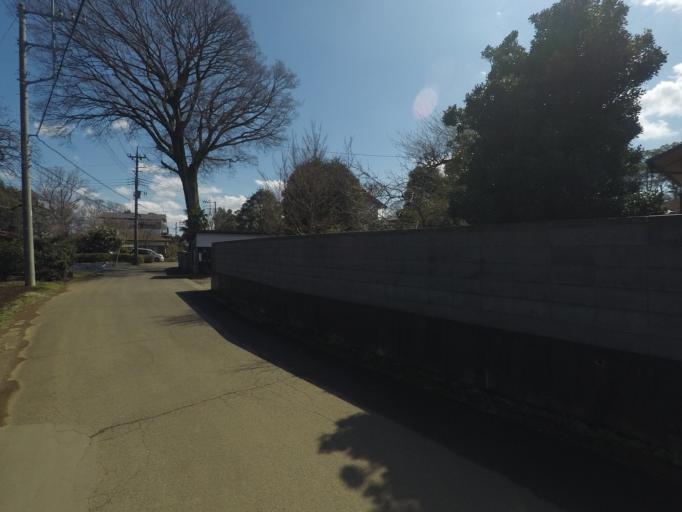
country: JP
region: Ibaraki
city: Ushiku
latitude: 36.0142
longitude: 140.0726
